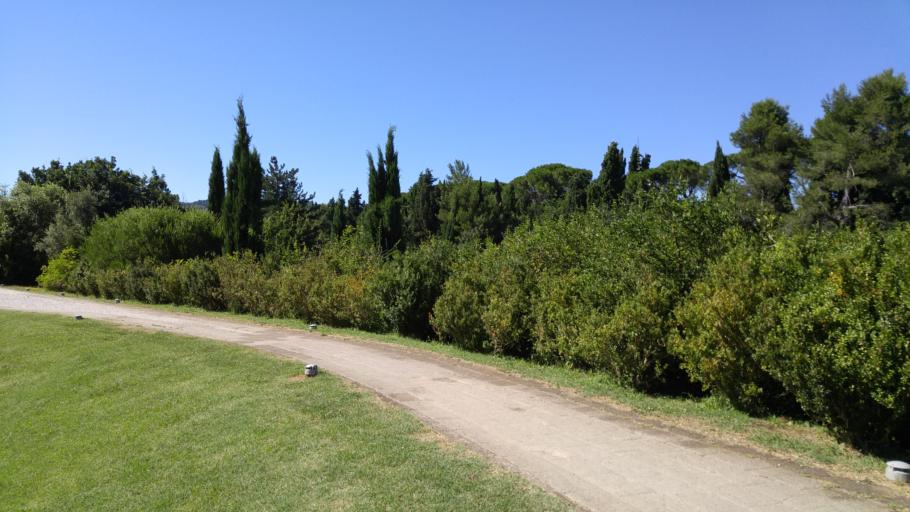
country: IT
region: The Marches
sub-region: Provincia di Pesaro e Urbino
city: Pesaro
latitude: 43.9043
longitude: 12.9011
